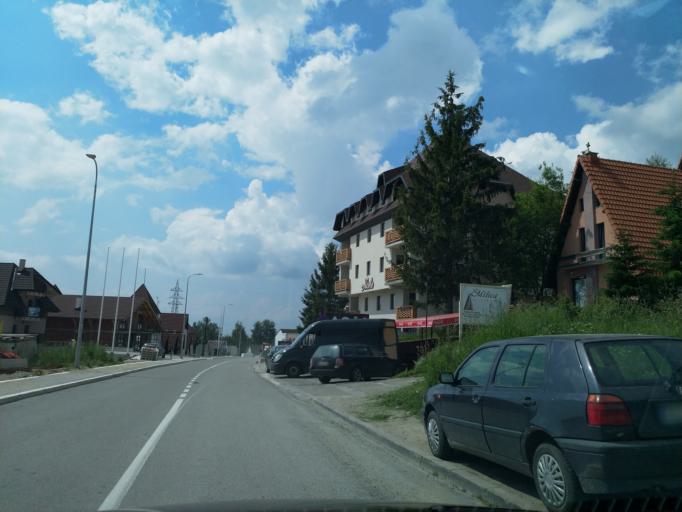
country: RS
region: Central Serbia
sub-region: Raski Okrug
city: Raska
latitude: 43.2741
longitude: 20.7678
